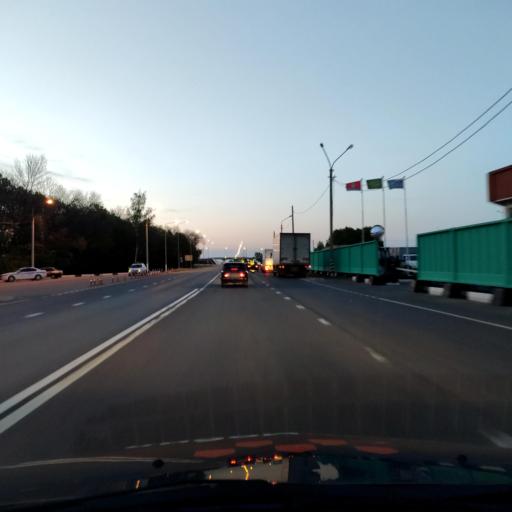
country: RU
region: Orjol
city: Zmiyevka
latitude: 52.7043
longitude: 36.3672
